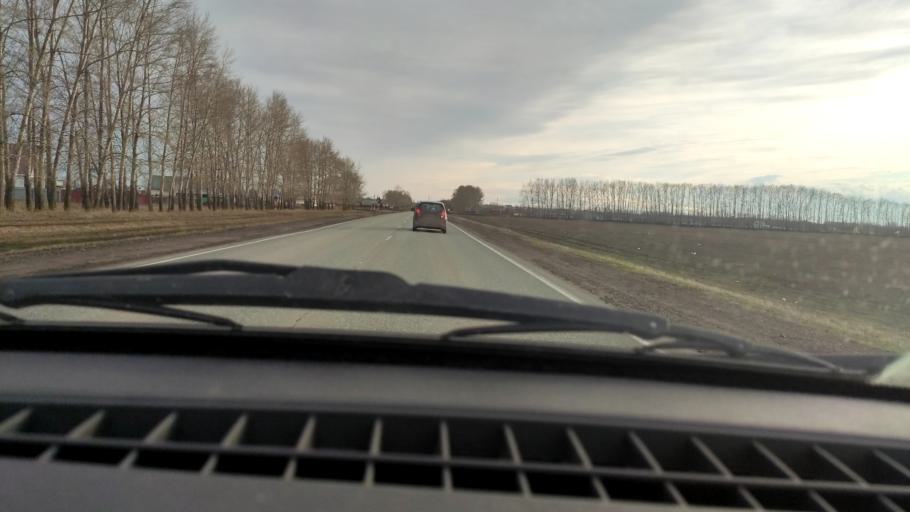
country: RU
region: Bashkortostan
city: Chishmy
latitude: 54.3964
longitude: 55.2085
